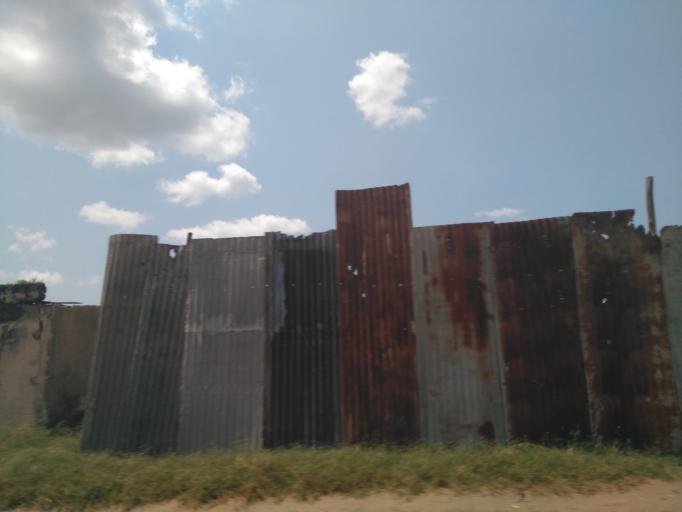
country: TZ
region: Dar es Salaam
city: Dar es Salaam
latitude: -6.8261
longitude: 39.3095
